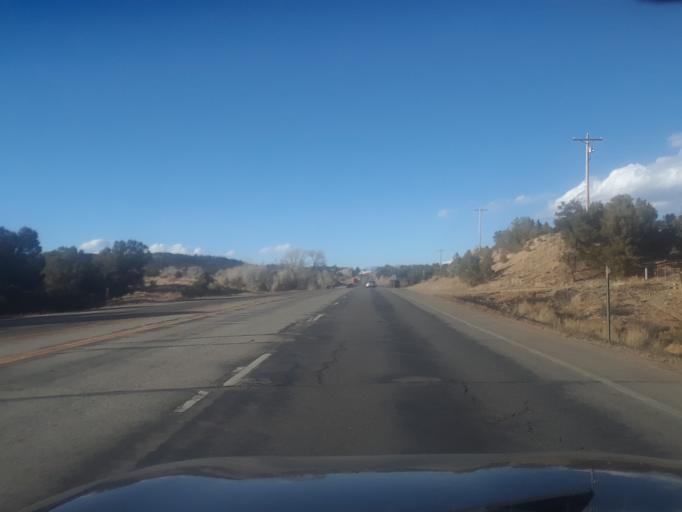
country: US
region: Colorado
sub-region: Chaffee County
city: Salida
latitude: 38.6610
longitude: -106.0878
